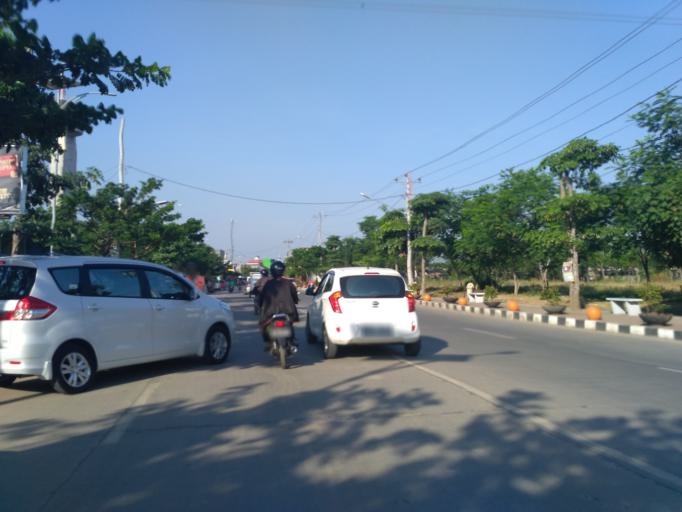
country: ID
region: Central Java
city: Semarang
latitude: -6.9858
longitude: 110.4441
